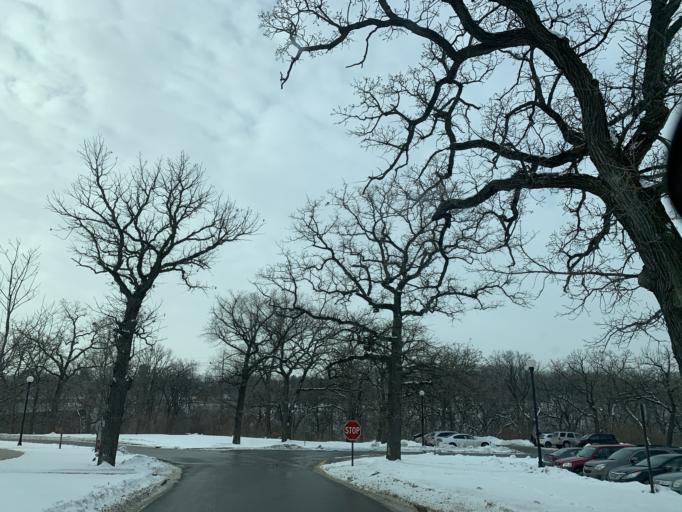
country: US
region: Minnesota
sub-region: Dakota County
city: Mendota Heights
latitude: 44.9139
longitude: -93.2050
